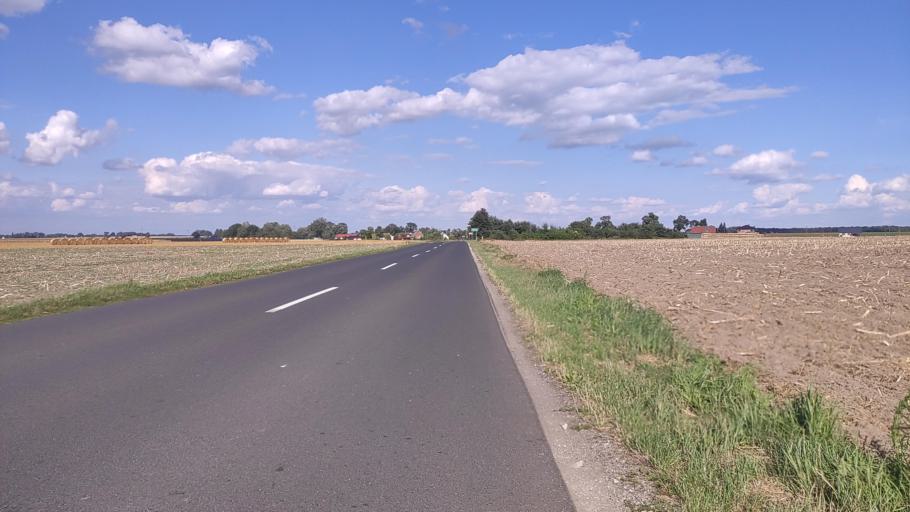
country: PL
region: Greater Poland Voivodeship
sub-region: Powiat poznanski
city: Swarzedz
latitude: 52.4214
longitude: 17.1472
